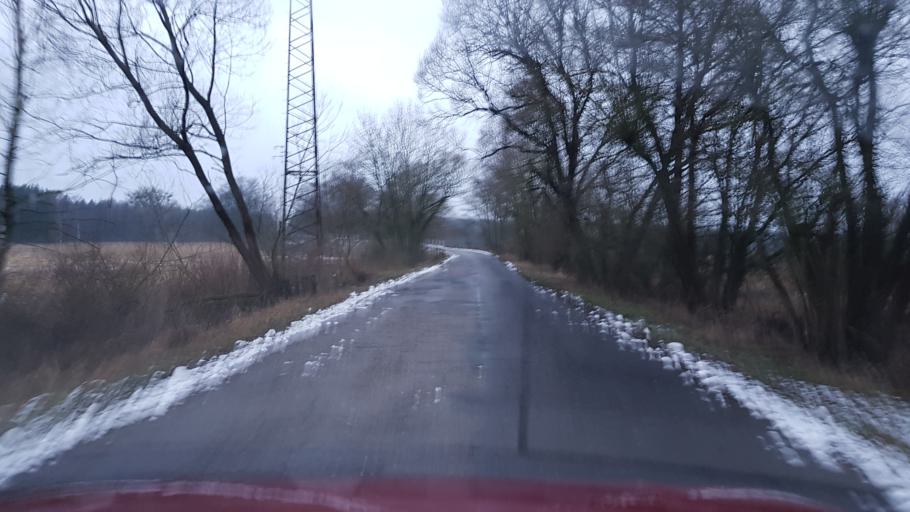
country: PL
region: West Pomeranian Voivodeship
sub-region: Powiat goleniowski
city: Goleniow
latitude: 53.4920
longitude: 14.8696
